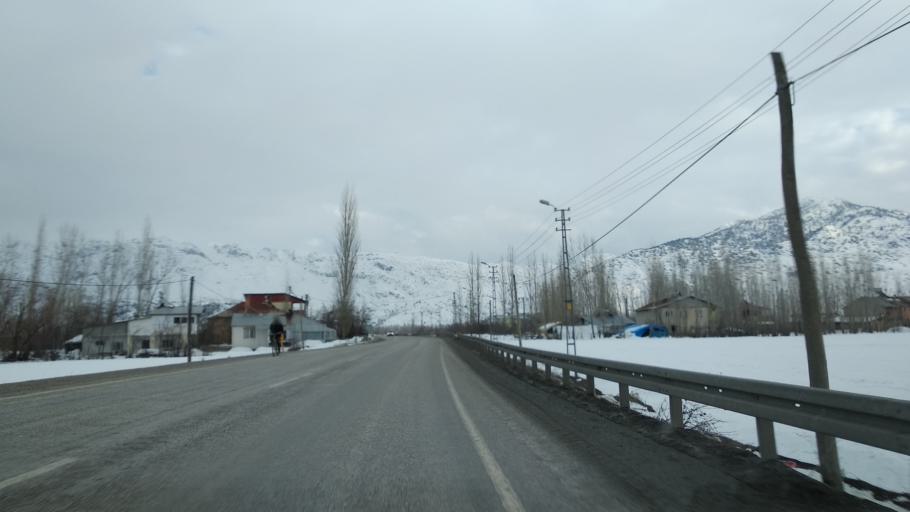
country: TR
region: Kahramanmaras
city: Goksun
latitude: 38.0116
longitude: 36.5068
